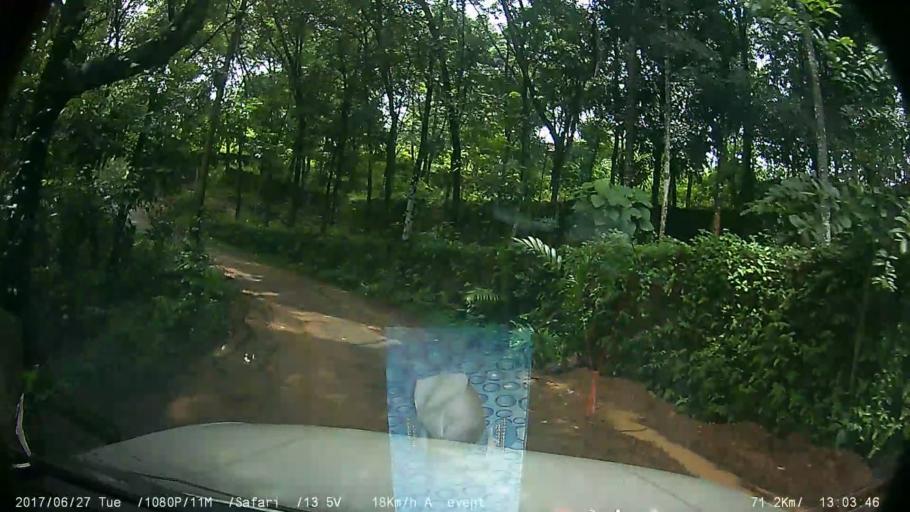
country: IN
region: Kerala
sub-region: Ernakulam
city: Piravam
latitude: 9.7832
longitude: 76.5438
